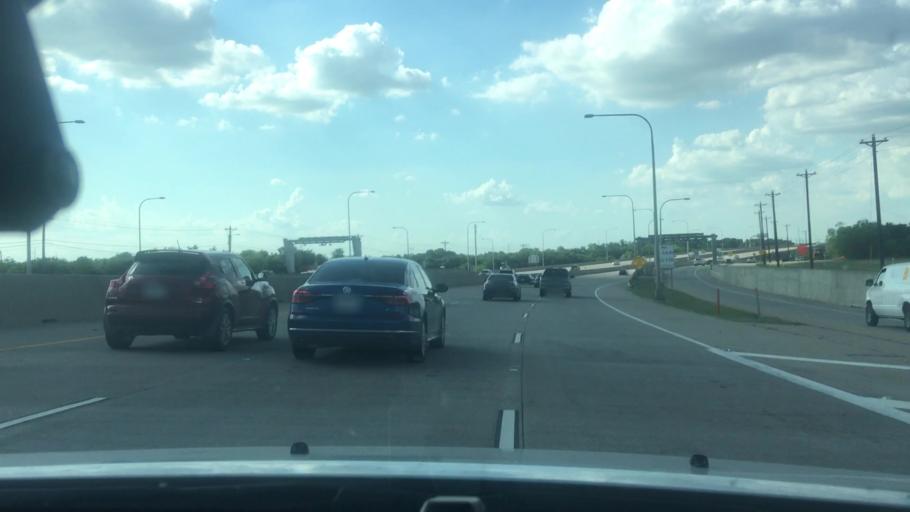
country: US
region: Texas
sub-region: Collin County
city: Frisco
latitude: 33.1397
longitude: -96.8376
